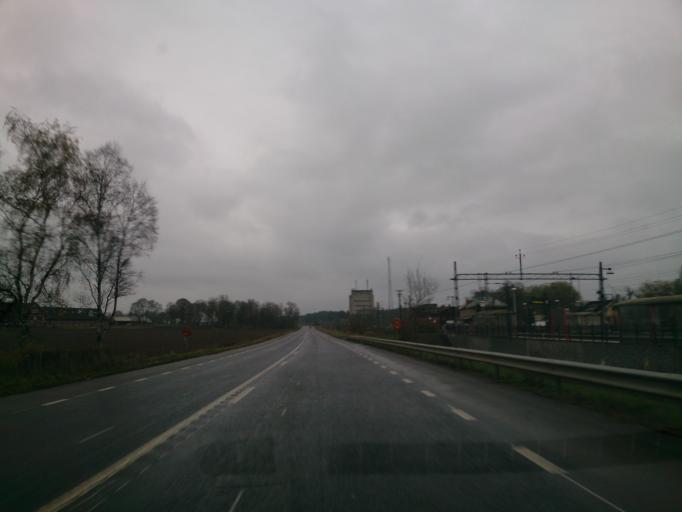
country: SE
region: OEstergoetland
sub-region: Linkopings Kommun
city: Linghem
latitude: 58.4365
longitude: 15.7845
